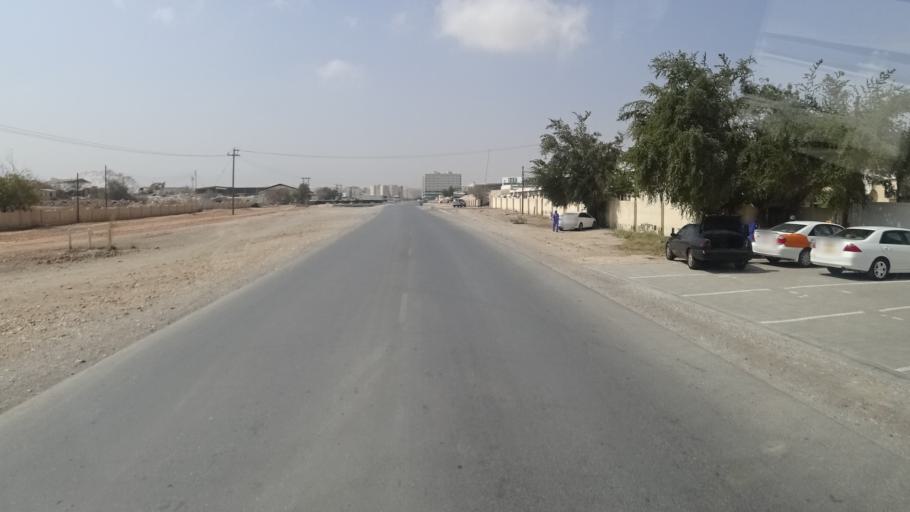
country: OM
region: Muhafazat Masqat
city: Bawshar
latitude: 23.5709
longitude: 58.3501
